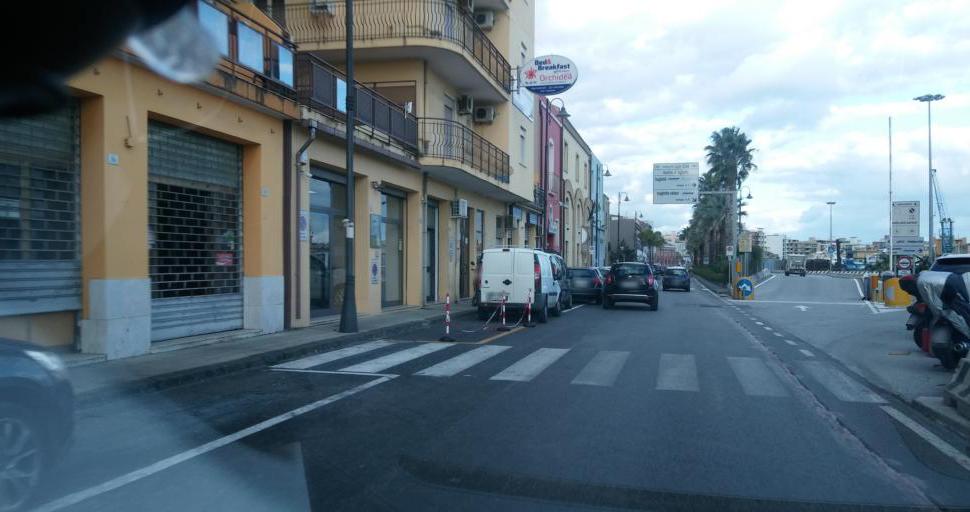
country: IT
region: Sicily
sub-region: Messina
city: Milazzo
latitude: 38.2140
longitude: 15.2439
